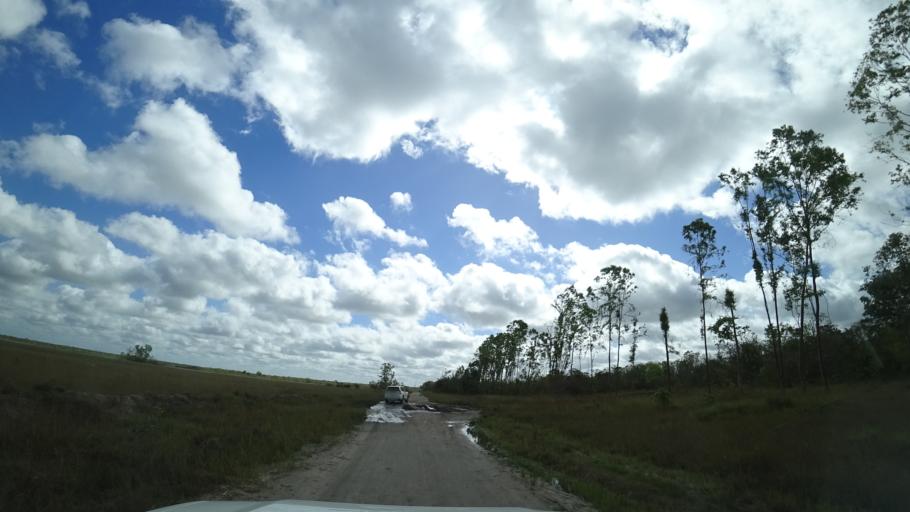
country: MZ
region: Sofala
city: Dondo
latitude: -19.6065
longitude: 35.0831
